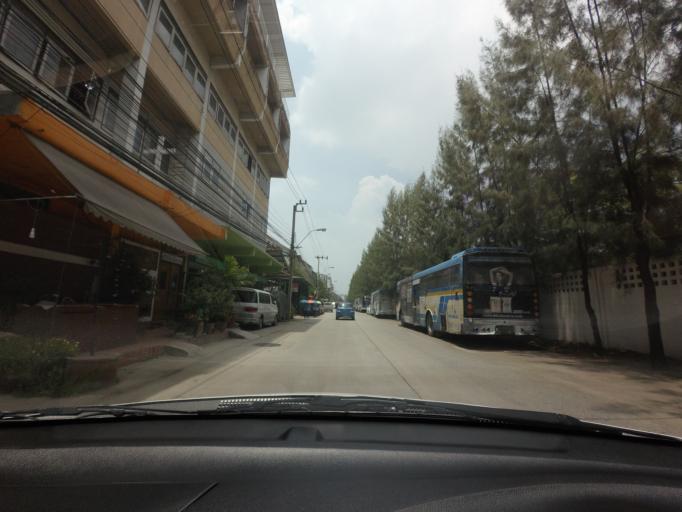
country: TH
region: Bangkok
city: Bang Na
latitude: 13.6659
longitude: 100.6865
